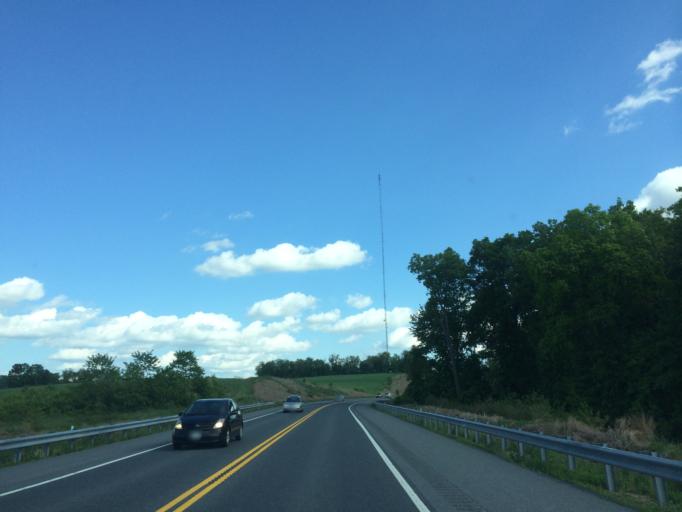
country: US
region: Maryland
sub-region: Carroll County
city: Hampstead
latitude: 39.6207
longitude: -76.8637
